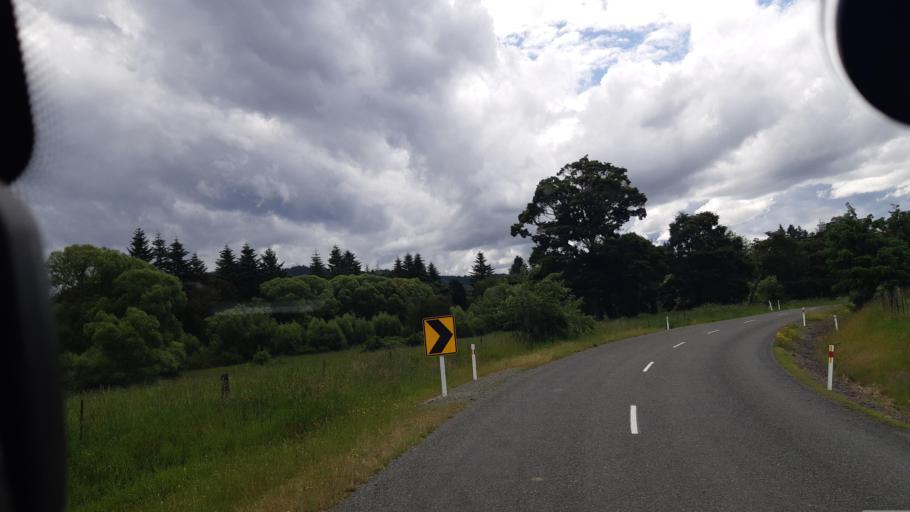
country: NZ
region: Tasman
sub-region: Tasman District
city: Wakefield
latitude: -41.6169
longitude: 172.8036
